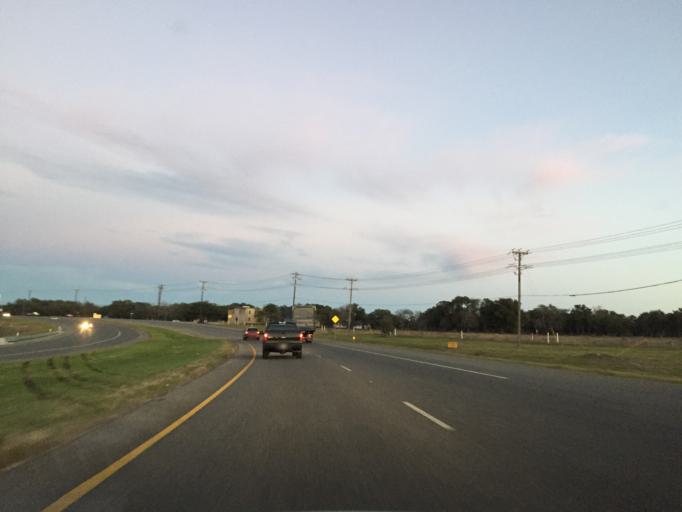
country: US
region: Texas
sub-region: Travis County
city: Jonestown
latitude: 30.5123
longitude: -97.8852
